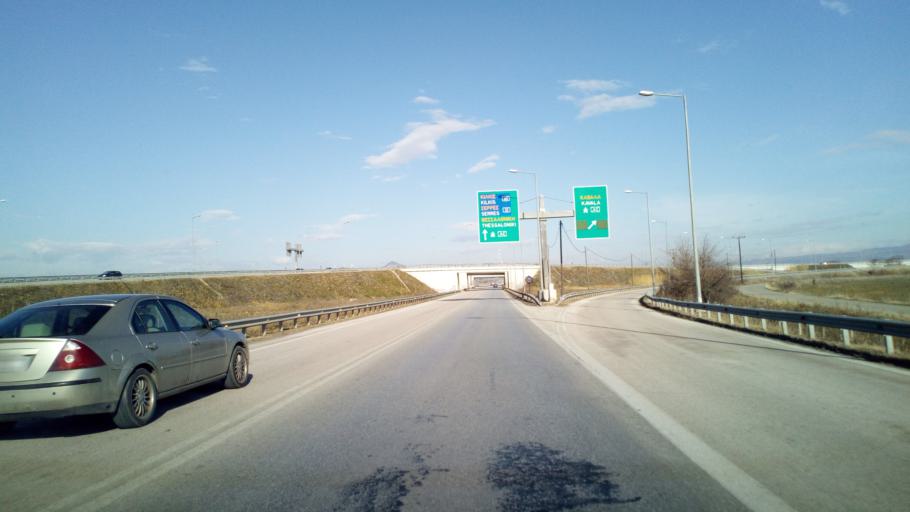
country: GR
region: Central Macedonia
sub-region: Nomos Thessalonikis
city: Lagyna
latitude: 40.7353
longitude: 23.0121
